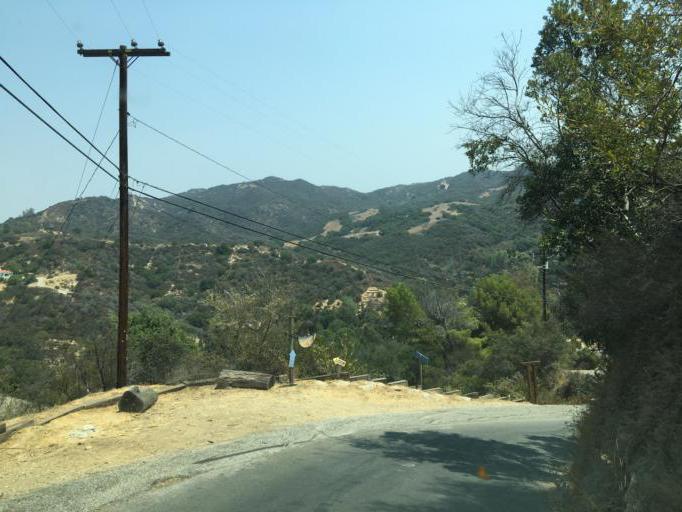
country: US
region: California
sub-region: Los Angeles County
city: Topanga
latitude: 34.1079
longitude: -118.5953
